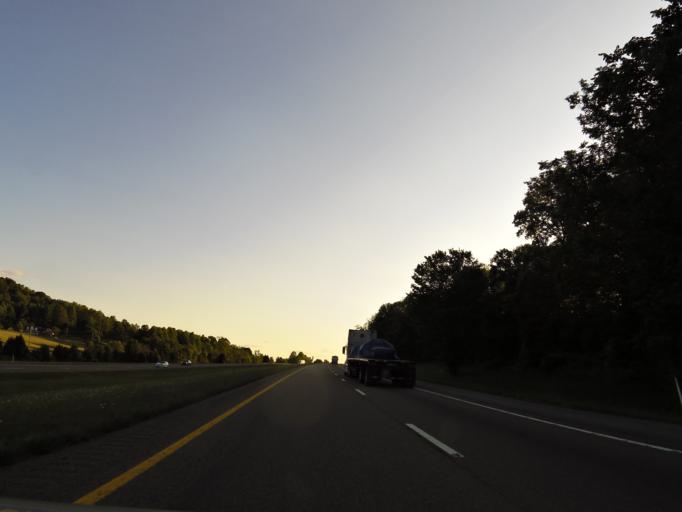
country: US
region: Tennessee
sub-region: Washington County
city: Spurgeon
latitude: 36.5142
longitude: -82.4127
